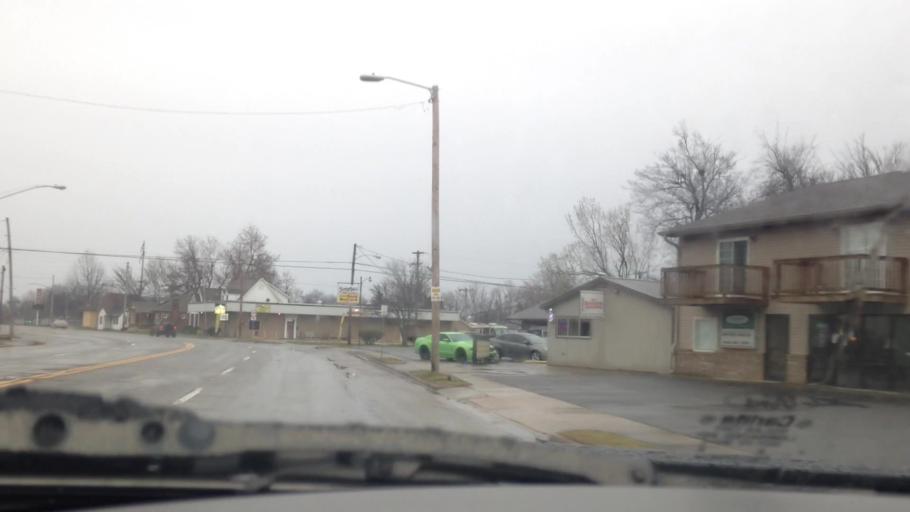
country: US
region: Illinois
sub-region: Massac County
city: Metropolis
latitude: 37.1464
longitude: -88.7236
